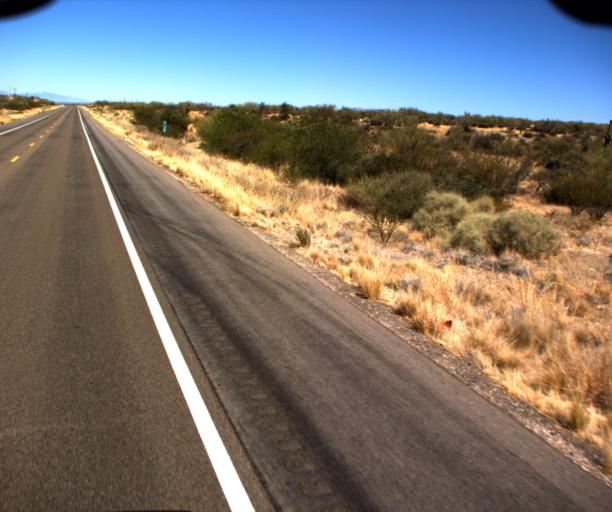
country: US
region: Arizona
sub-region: Pima County
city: Three Points
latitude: 32.0373
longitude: -111.5182
